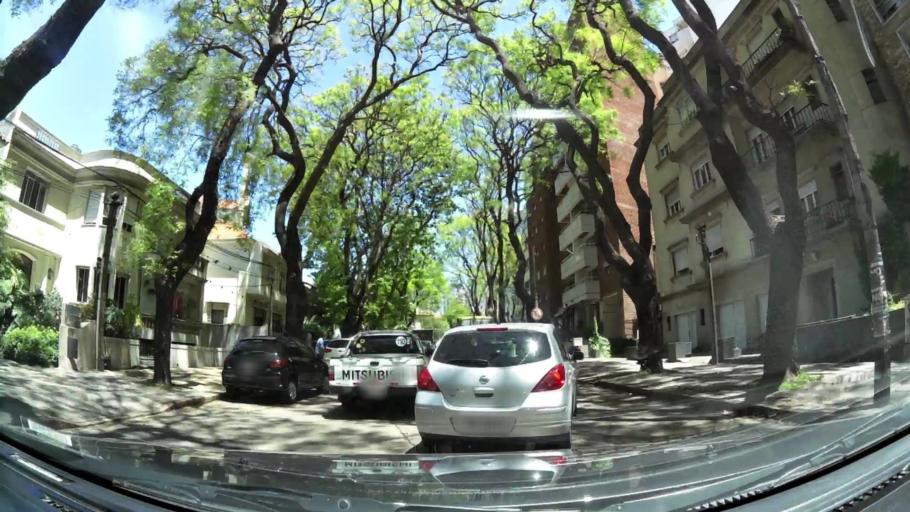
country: UY
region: Montevideo
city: Montevideo
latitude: -34.9125
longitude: -56.1529
